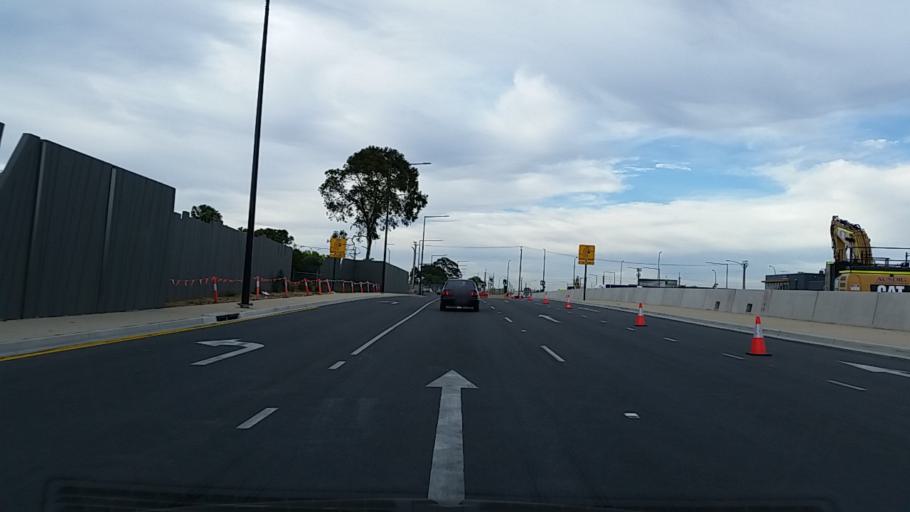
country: AU
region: South Australia
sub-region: City of West Torrens
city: Thebarton
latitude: -34.9061
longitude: 138.5651
